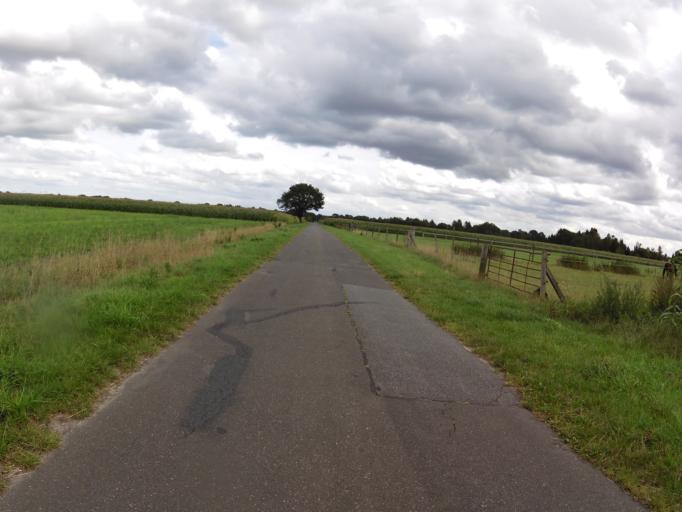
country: DE
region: Lower Saxony
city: Kohlen
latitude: 53.5122
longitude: 8.8510
